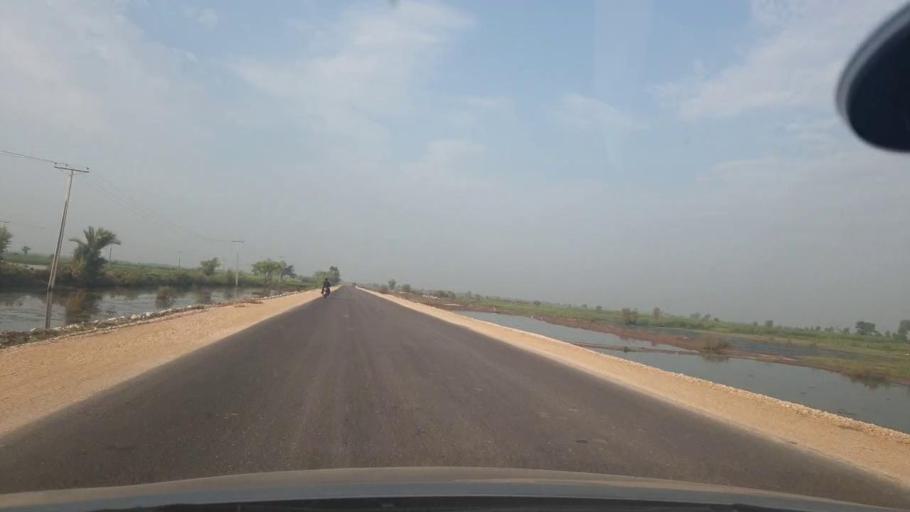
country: PK
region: Sindh
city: Jacobabad
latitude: 28.2293
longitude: 68.3824
